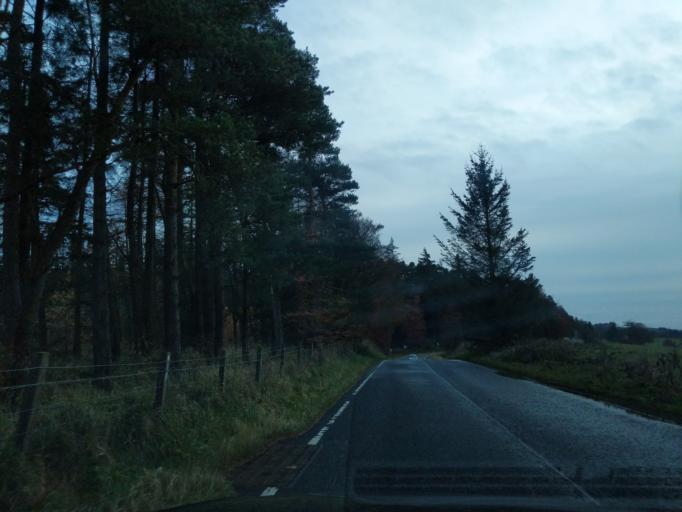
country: GB
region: Scotland
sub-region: West Lothian
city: Linlithgow
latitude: 55.9461
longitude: -3.6157
